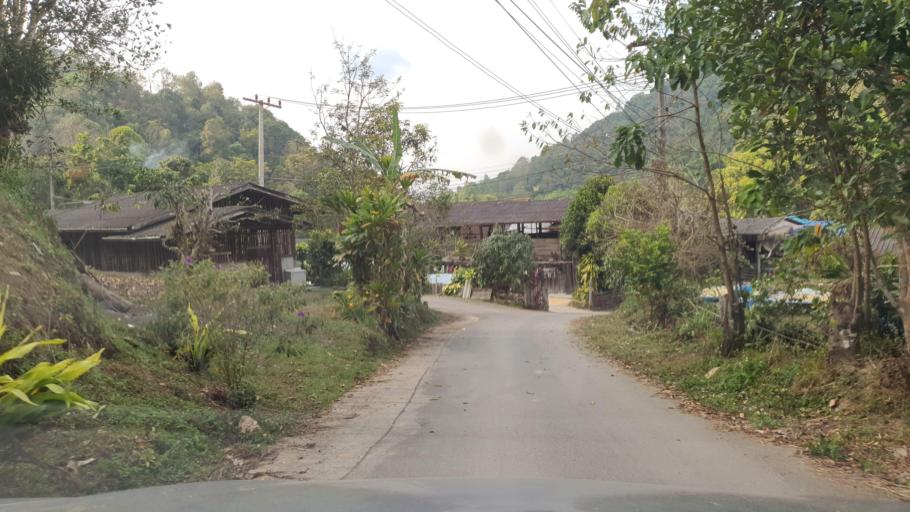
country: TH
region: Chiang Mai
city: Mae On
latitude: 18.9451
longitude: 99.3587
